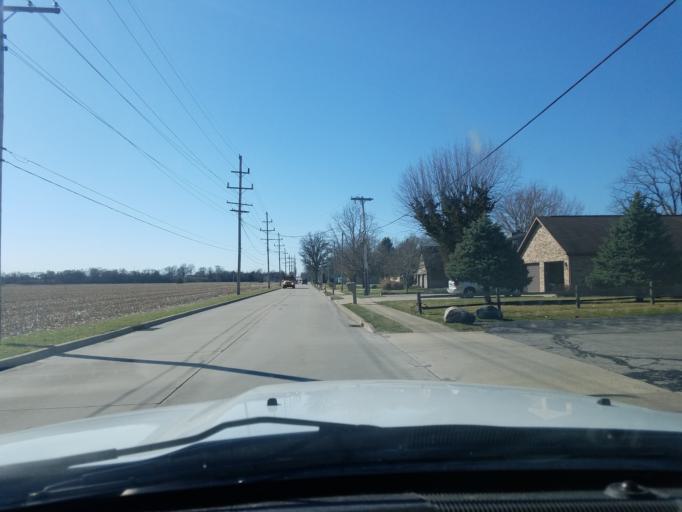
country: US
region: Indiana
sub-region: Shelby County
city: Shelbyville
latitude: 39.5048
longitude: -85.7747
